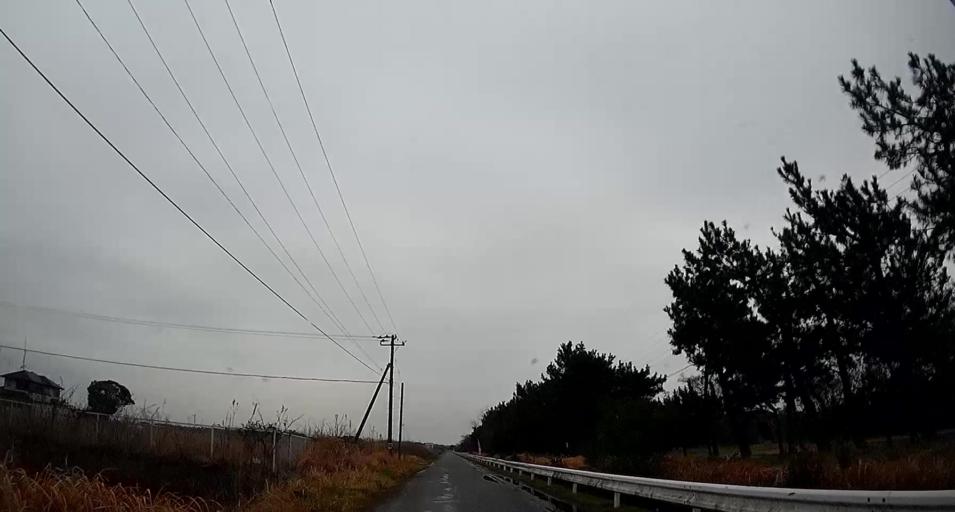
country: JP
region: Chiba
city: Kisarazu
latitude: 35.4061
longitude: 139.9078
